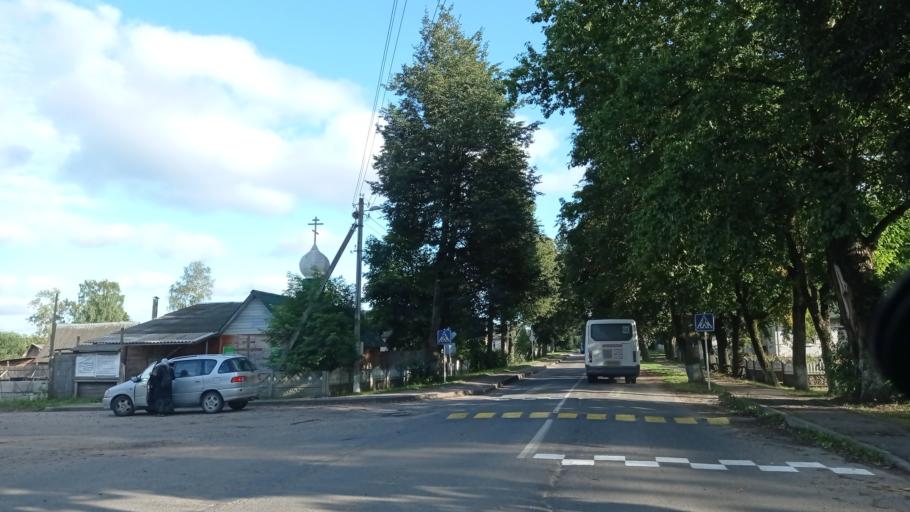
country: BY
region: Vitebsk
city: Vitebsk
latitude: 55.2062
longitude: 30.2883
